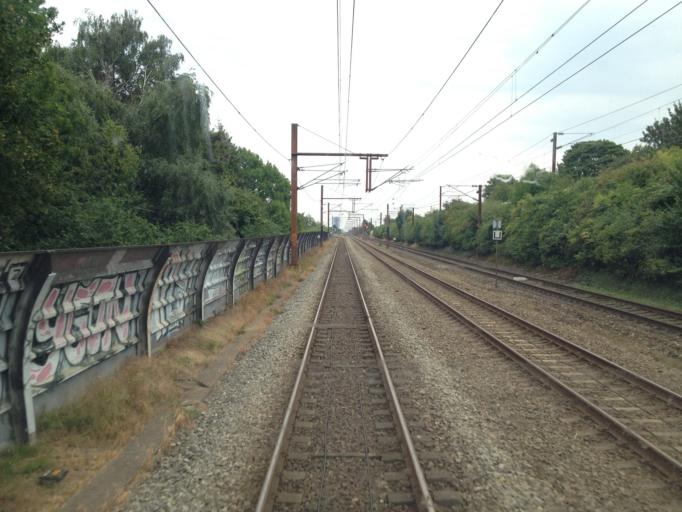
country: DK
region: Capital Region
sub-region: Hvidovre Kommune
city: Hvidovre
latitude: 55.6644
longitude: 12.4866
